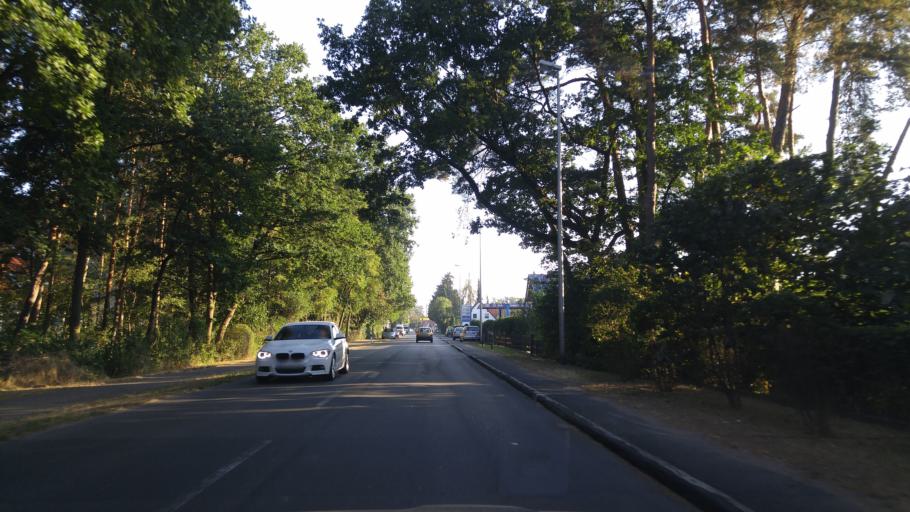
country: DE
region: Bavaria
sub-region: Regierungsbezirk Mittelfranken
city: Erlangen
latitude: 49.5485
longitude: 10.9866
